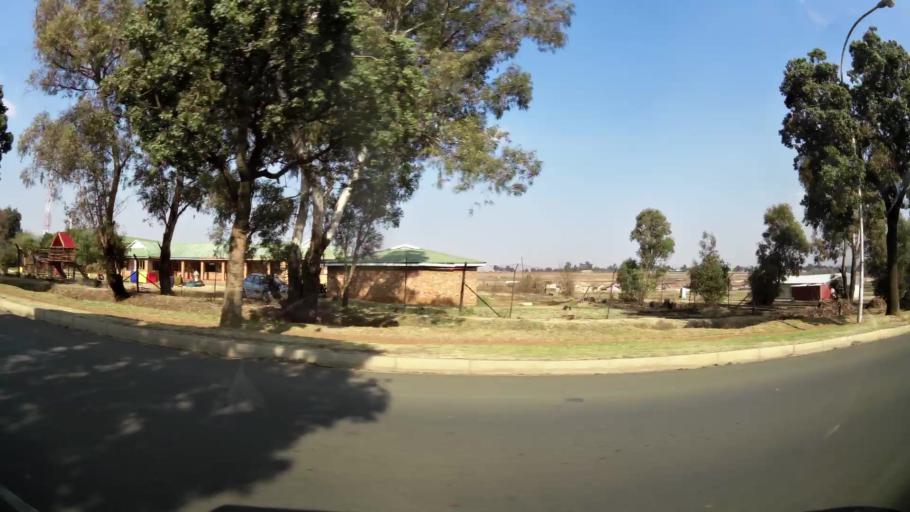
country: ZA
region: Gauteng
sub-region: Ekurhuleni Metropolitan Municipality
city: Brakpan
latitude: -26.1607
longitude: 28.4079
